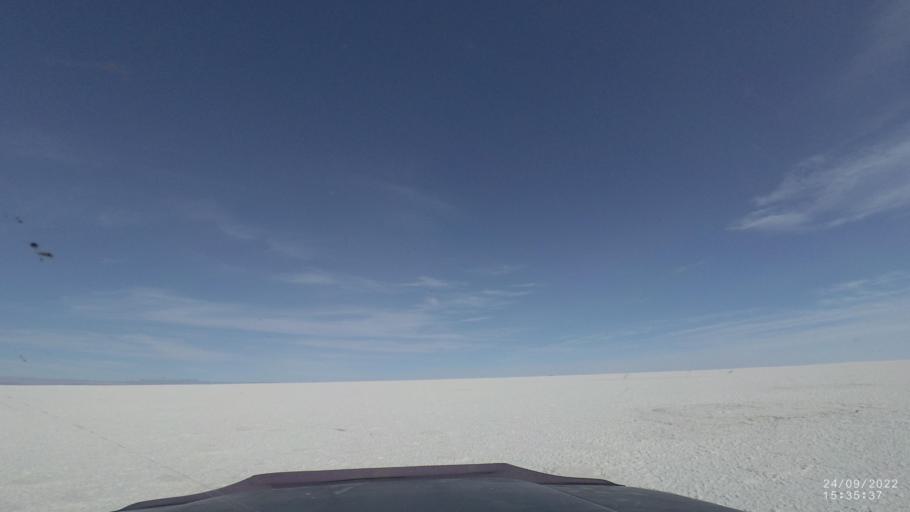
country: BO
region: Potosi
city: Colchani
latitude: -20.1374
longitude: -67.2524
